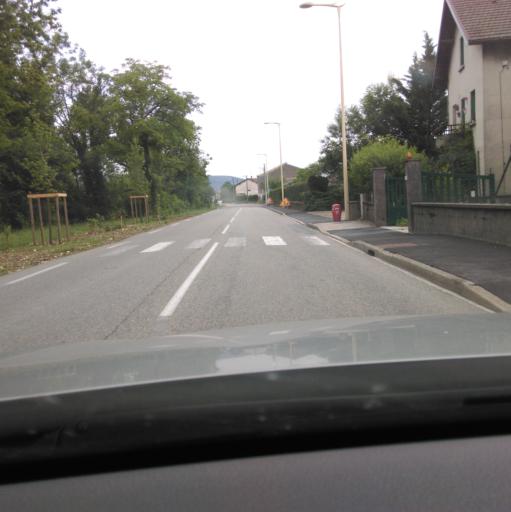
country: FR
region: Rhone-Alpes
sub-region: Departement de l'Ain
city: Izernore
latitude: 46.1896
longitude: 5.5436
